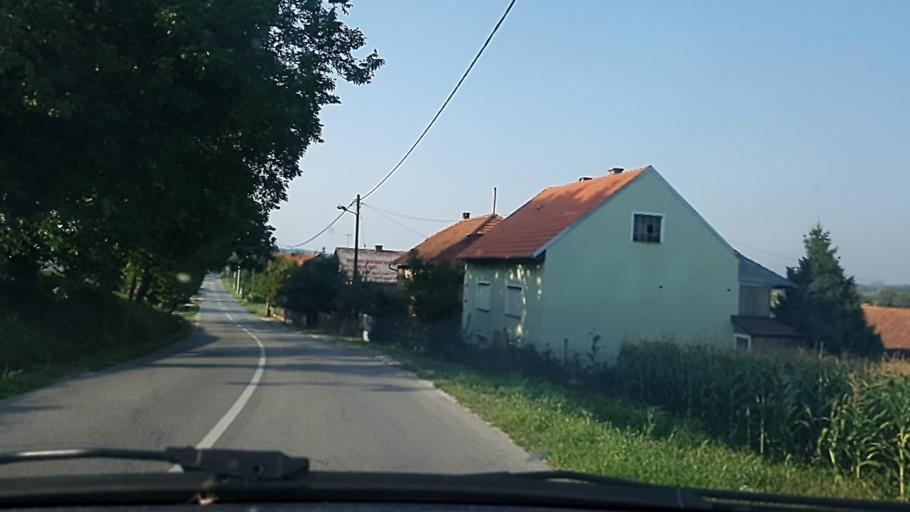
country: HR
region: Zagrebacka
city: Pojatno
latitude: 45.9266
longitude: 15.8155
